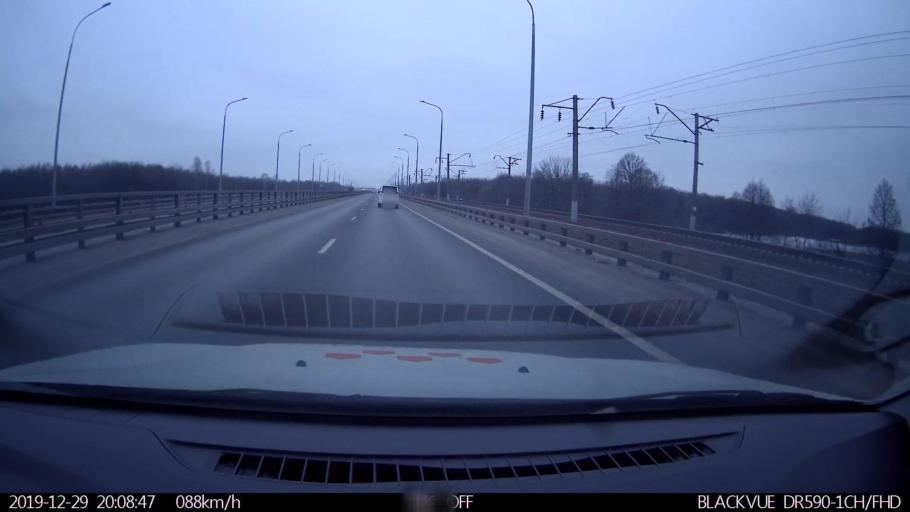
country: RU
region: Nizjnij Novgorod
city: Neklyudovo
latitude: 56.3813
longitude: 43.9597
